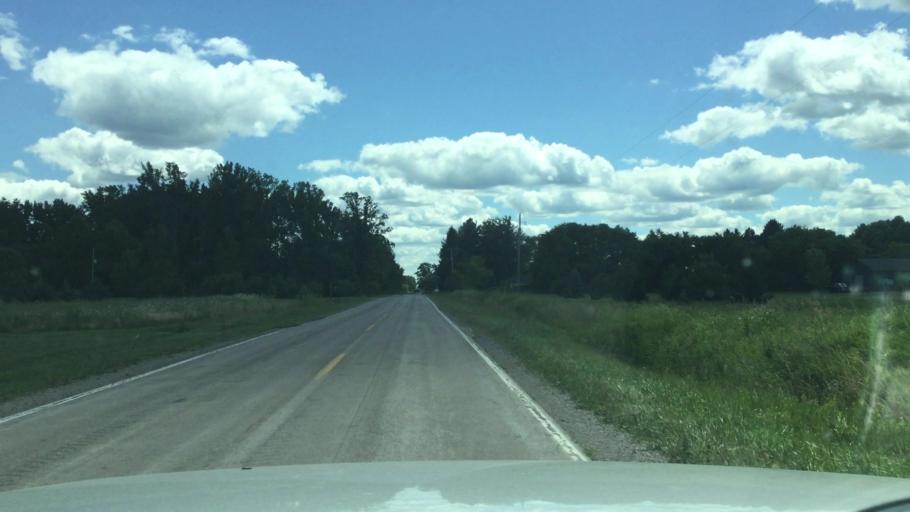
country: US
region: Michigan
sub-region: Saginaw County
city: Hemlock
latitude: 43.3545
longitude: -84.1901
